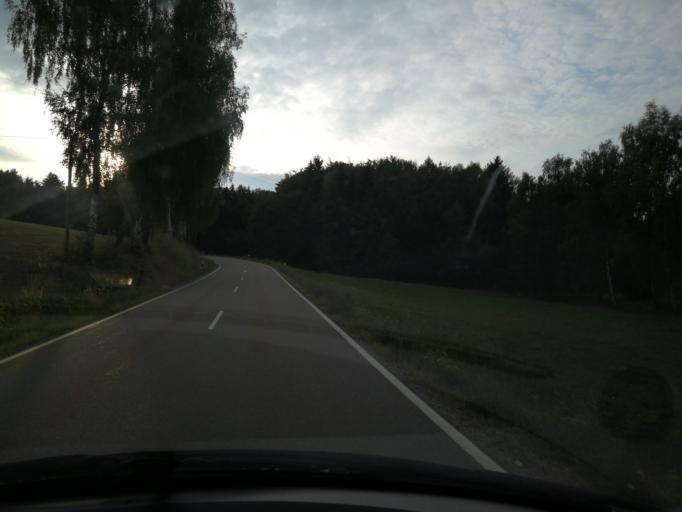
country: DE
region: Bavaria
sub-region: Lower Bavaria
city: Falkenfels
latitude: 49.0436
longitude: 12.6009
